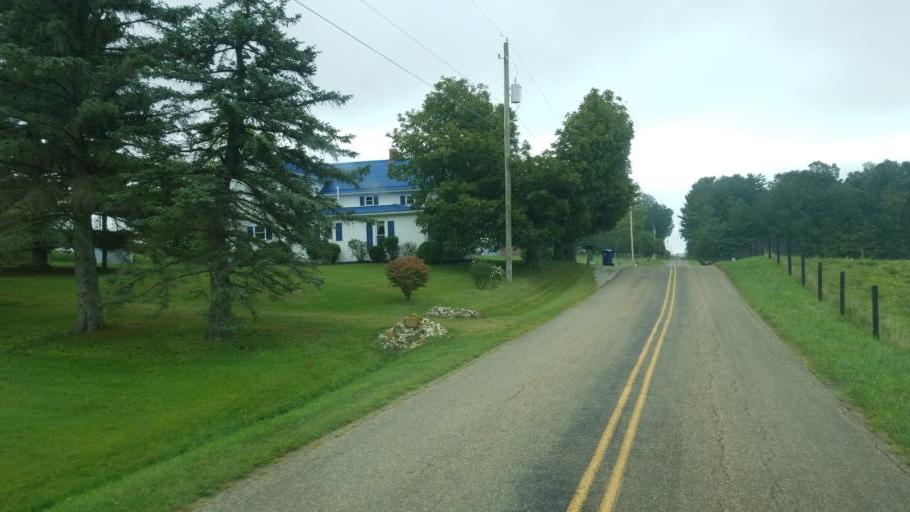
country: US
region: Ohio
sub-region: Licking County
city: Utica
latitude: 40.2799
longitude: -82.4054
